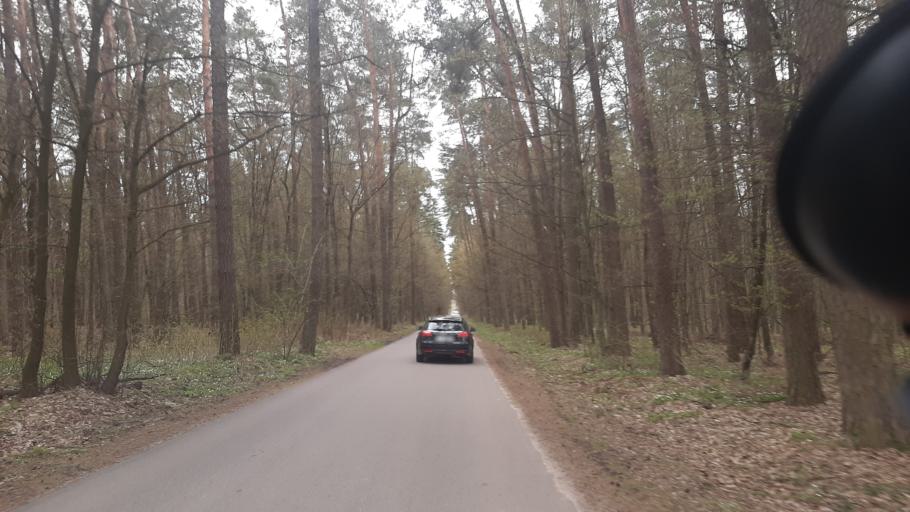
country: PL
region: Lublin Voivodeship
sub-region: Powiat lubelski
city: Niemce
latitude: 51.3739
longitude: 22.5527
